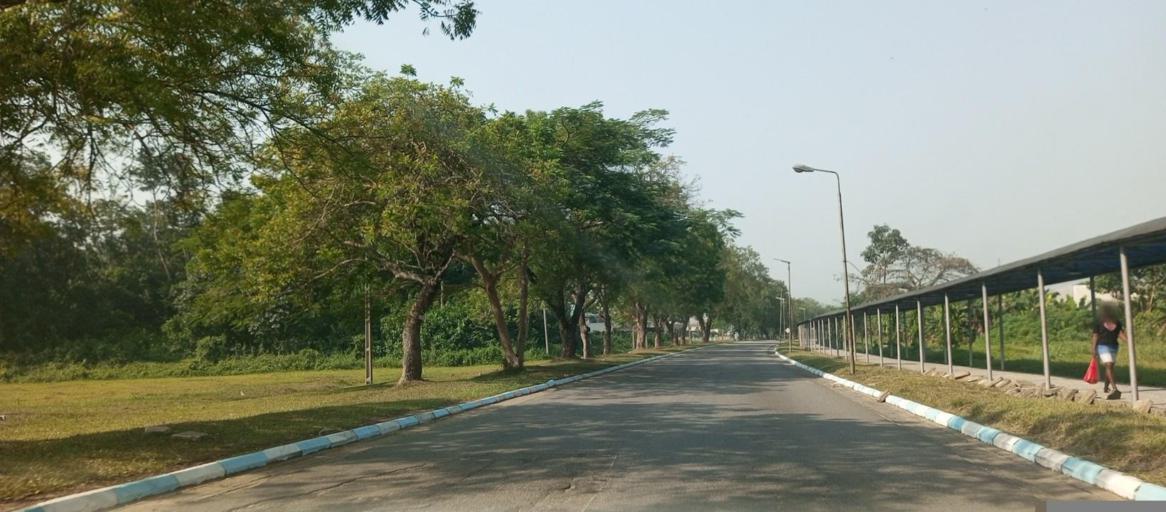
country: NG
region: Rivers
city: Emuoha
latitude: 4.9033
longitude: 6.9123
